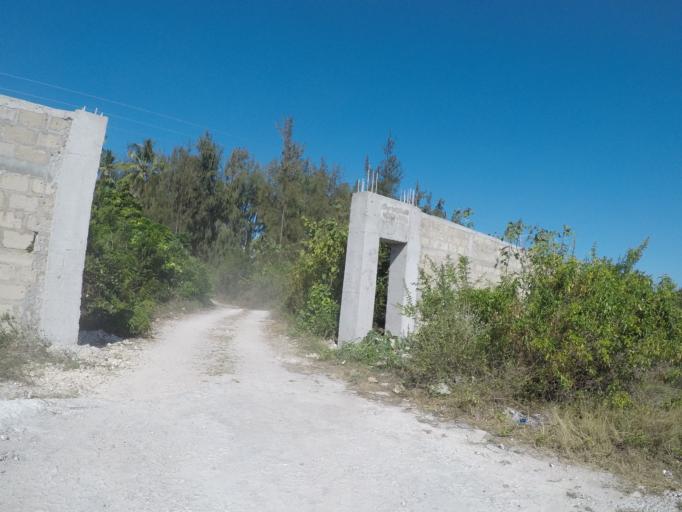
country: TZ
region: Zanzibar Central/South
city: Nganane
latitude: -6.2767
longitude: 39.5341
